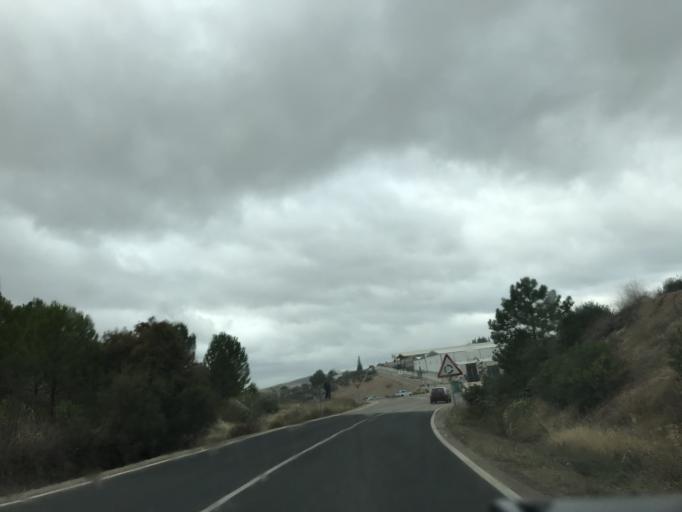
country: ES
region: Andalusia
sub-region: Provincia de Jaen
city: Peal de Becerro
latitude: 37.9179
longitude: -3.1303
